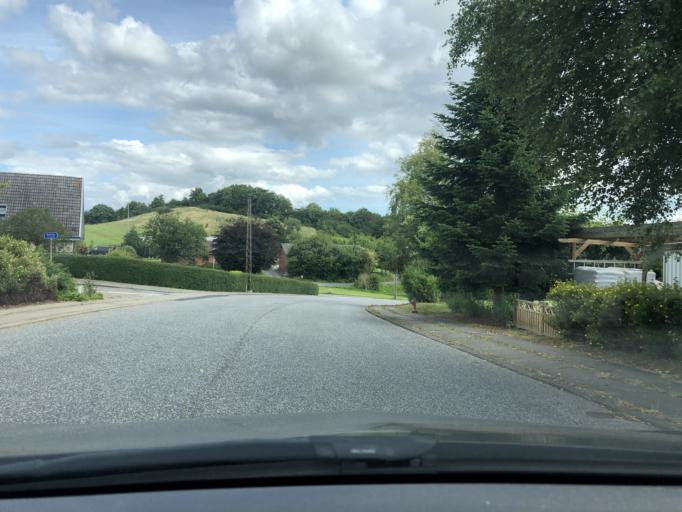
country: DK
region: South Denmark
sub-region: Vejle Kommune
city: Vejle
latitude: 55.6919
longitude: 9.4643
